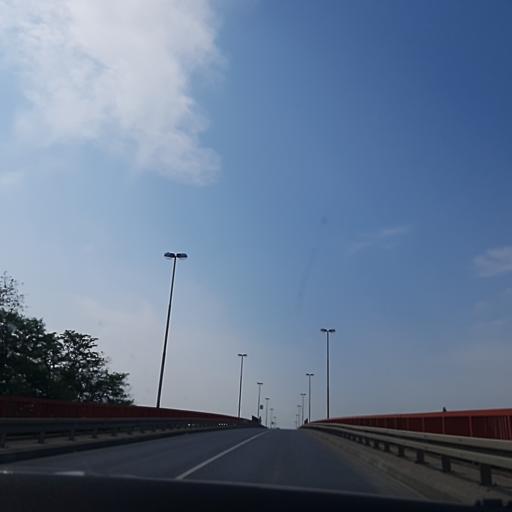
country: RS
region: Autonomna Pokrajina Vojvodina
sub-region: Juznobanatski Okrug
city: Pancevo
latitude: 44.8885
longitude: 20.6311
